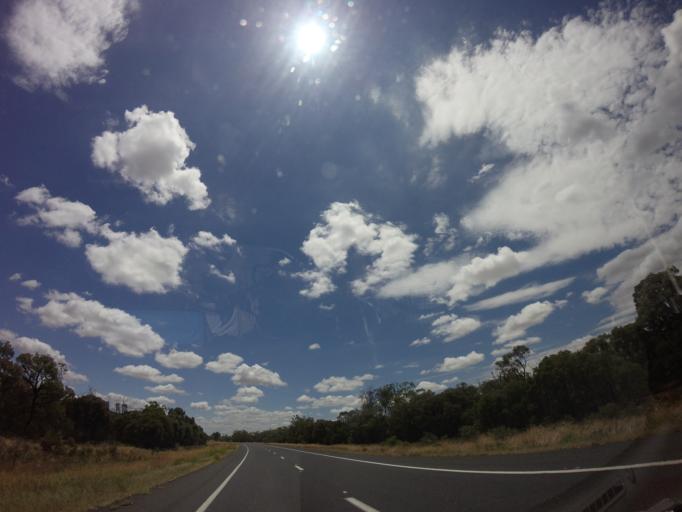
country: AU
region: New South Wales
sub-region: Moree Plains
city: Boggabilla
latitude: -28.8595
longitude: 150.2129
